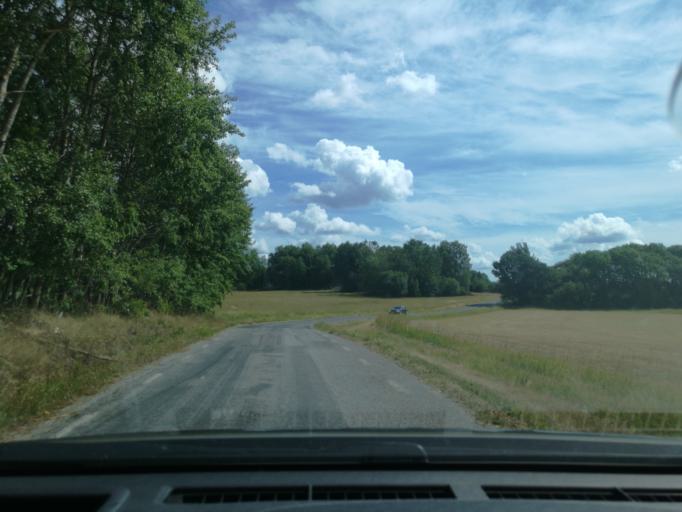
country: SE
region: Stockholm
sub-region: Sigtuna Kommun
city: Marsta
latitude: 59.6510
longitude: 17.8809
